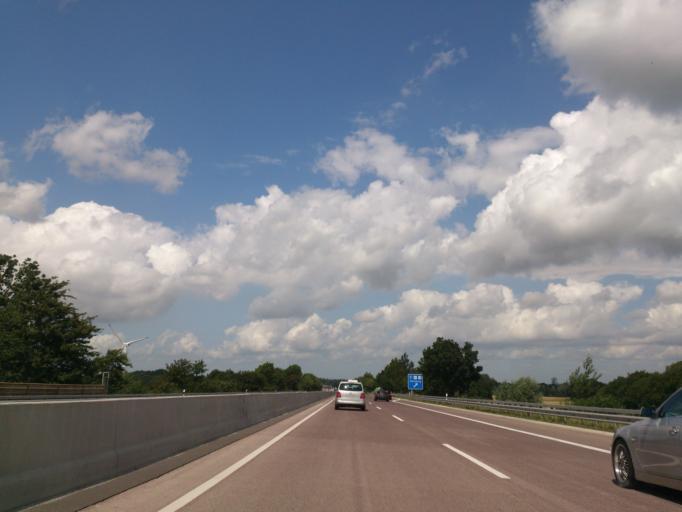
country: DE
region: Schleswig-Holstein
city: Horst
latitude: 53.8255
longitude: 9.6396
